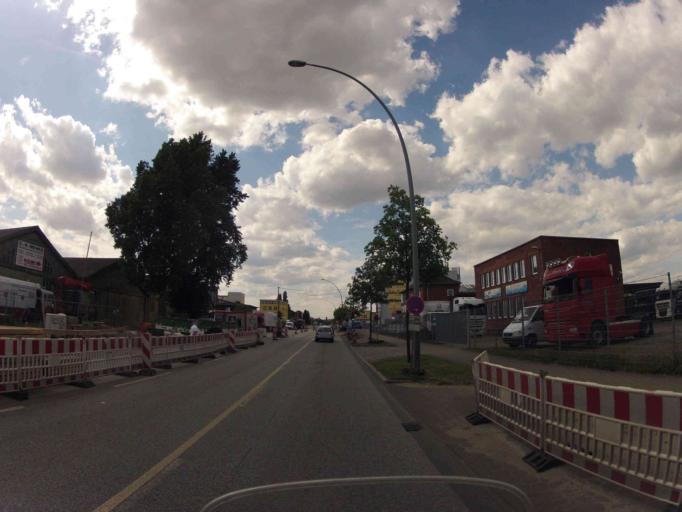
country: DE
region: Hamburg
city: Rothenburgsort
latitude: 53.5369
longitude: 10.0620
